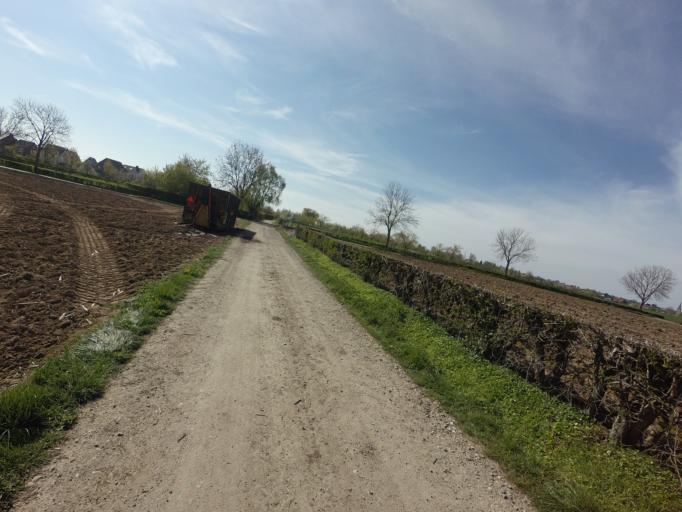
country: NL
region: Limburg
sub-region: Eijsden-Margraten
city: Eijsden
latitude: 50.7993
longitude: 5.7692
